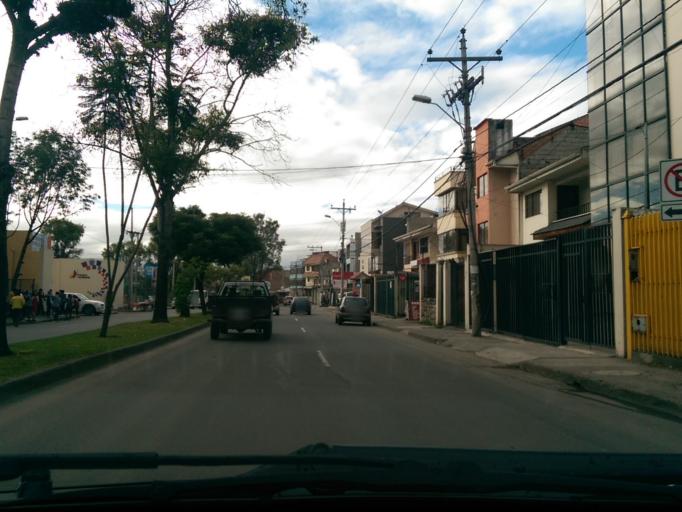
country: EC
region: Azuay
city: Cuenca
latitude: -2.8943
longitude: -79.0211
